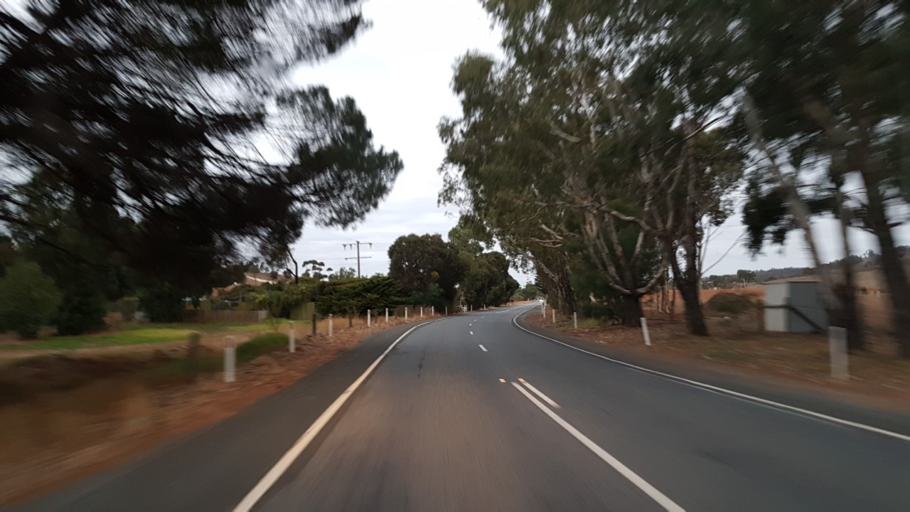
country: AU
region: South Australia
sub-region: Mount Barker
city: Callington
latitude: -35.0589
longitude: 139.0116
